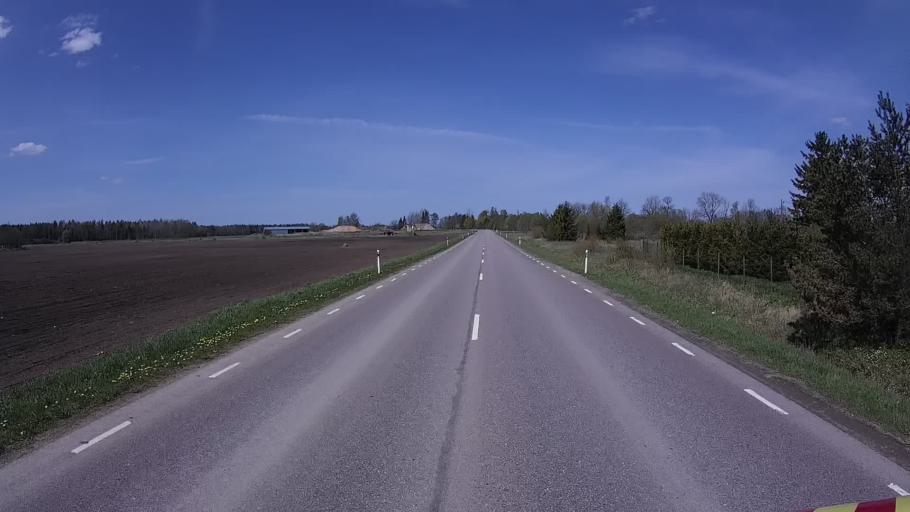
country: EE
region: Harju
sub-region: Keila linn
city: Keila
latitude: 59.3065
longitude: 24.3231
